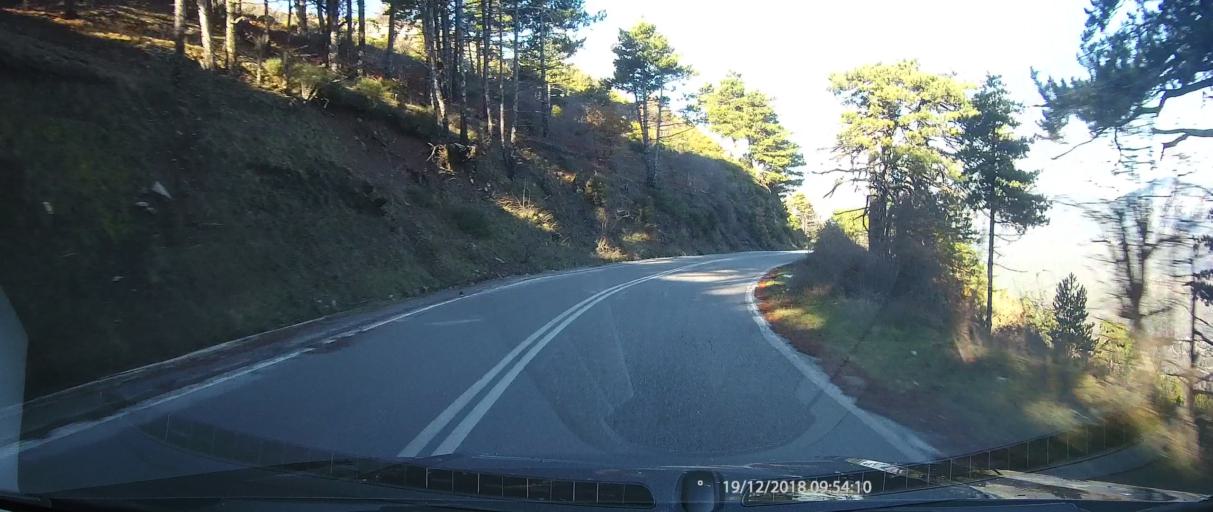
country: GR
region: Peloponnese
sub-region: Nomos Messinias
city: Paralia Vergas
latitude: 37.0788
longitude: 22.2495
